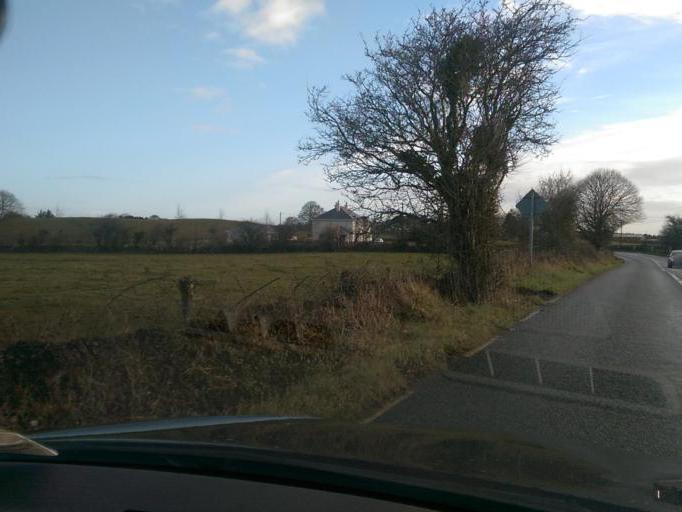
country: IE
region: Connaught
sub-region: County Galway
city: Athenry
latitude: 53.3669
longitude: -8.7174
